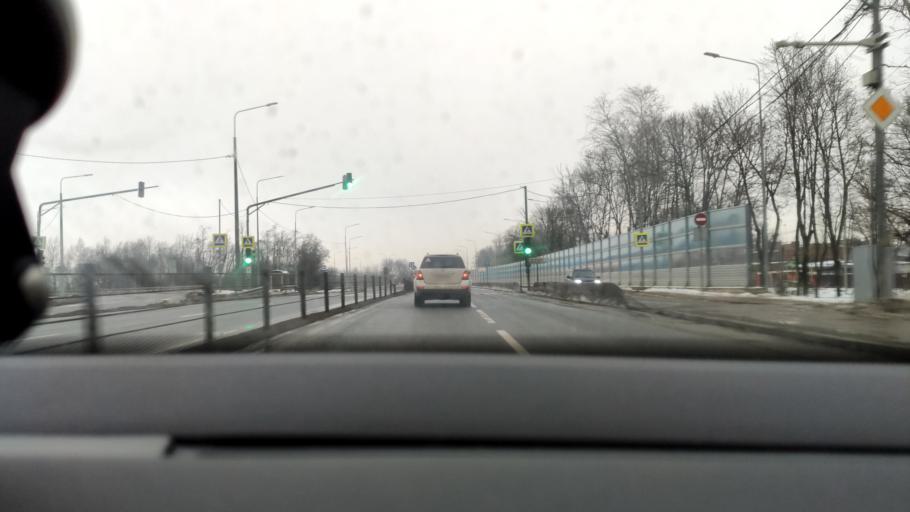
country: RU
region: Moskovskaya
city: Sergiyev Posad
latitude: 56.2703
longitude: 38.1209
